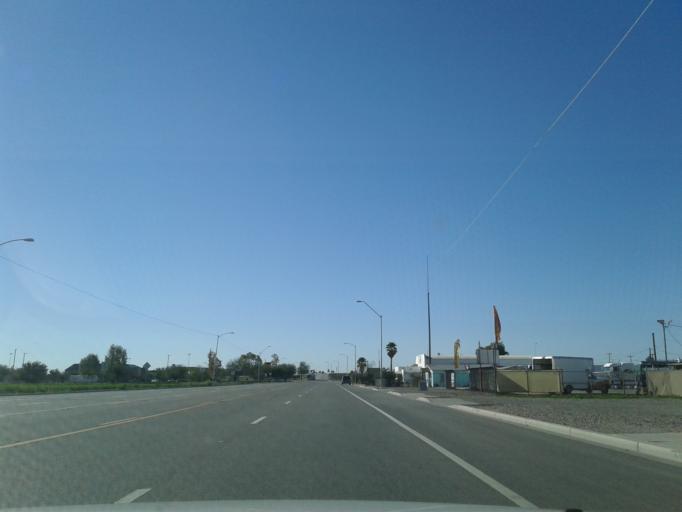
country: US
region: Arizona
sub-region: Pinal County
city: Eloy
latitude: 32.7415
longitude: -111.5505
